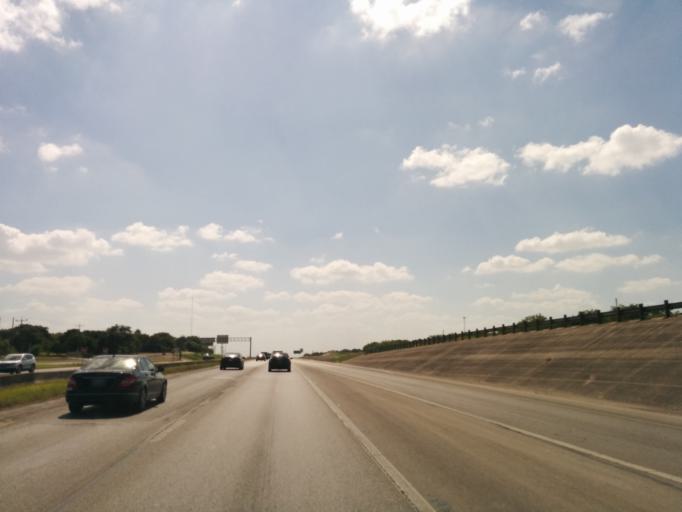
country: US
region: Texas
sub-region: Bexar County
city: Live Oak
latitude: 29.6029
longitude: -98.3718
